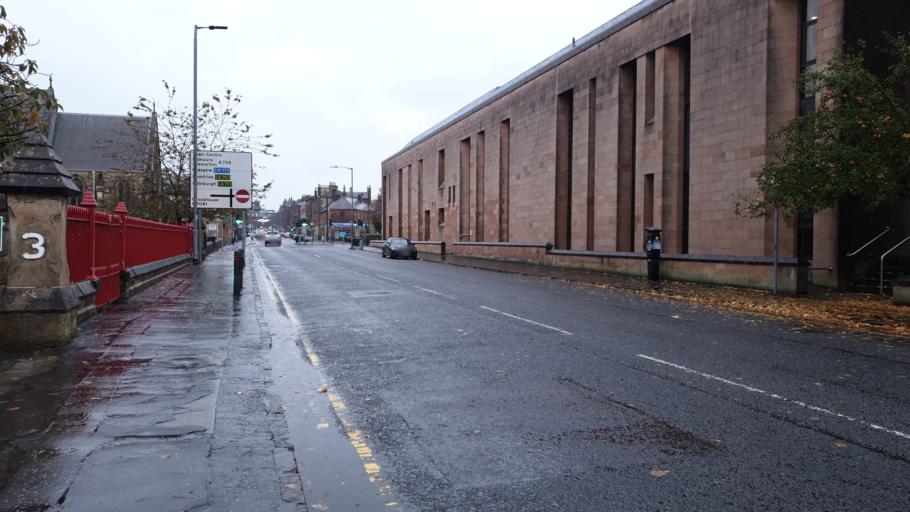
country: GB
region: Scotland
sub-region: East Ayrshire
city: Kilmarnock
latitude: 55.6069
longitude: -4.5003
